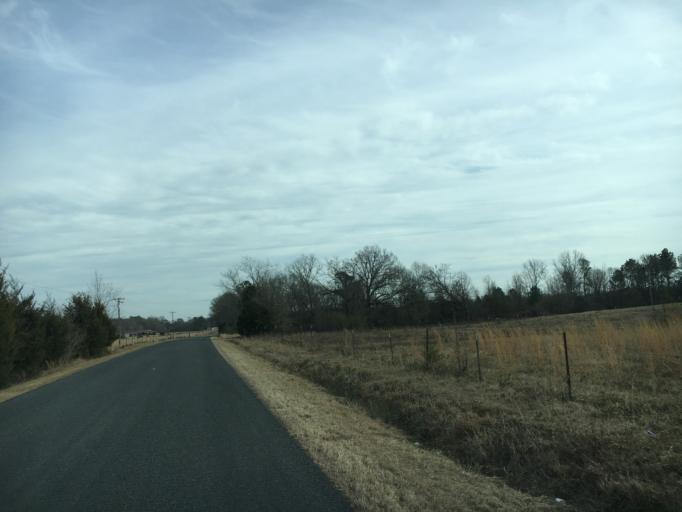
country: US
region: South Carolina
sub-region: Laurens County
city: Laurens
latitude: 34.3661
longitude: -81.9839
